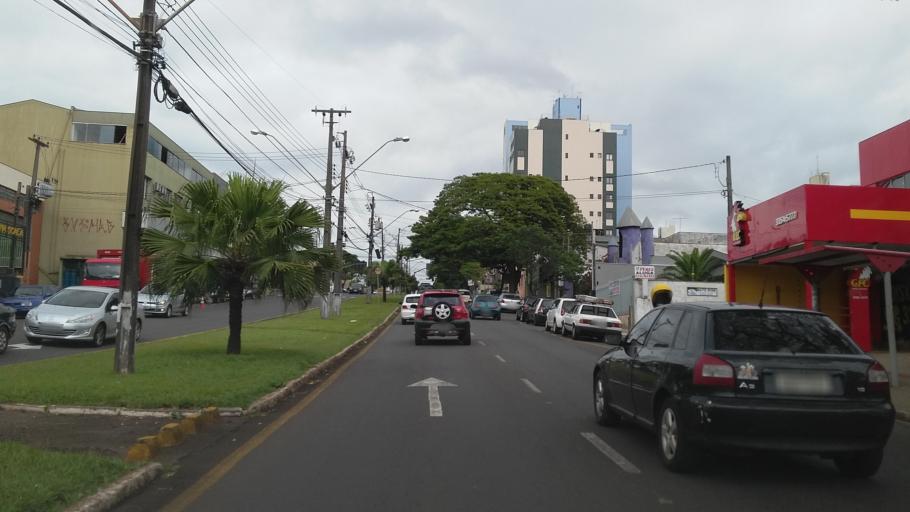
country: BR
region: Parana
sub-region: Londrina
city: Londrina
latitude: -23.3198
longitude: -51.1539
